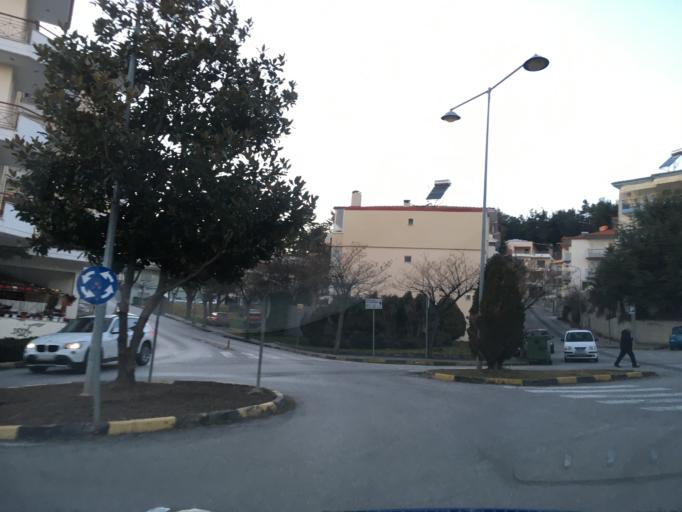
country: GR
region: West Macedonia
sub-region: Nomos Kozanis
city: Kozani
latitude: 40.3035
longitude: 21.7959
